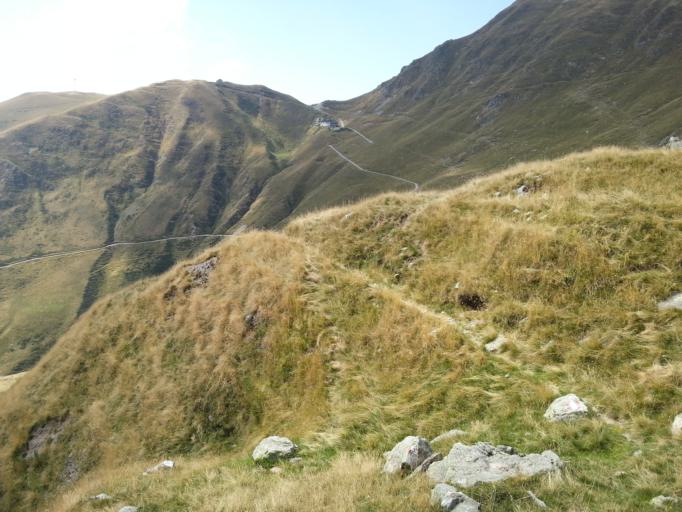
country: CH
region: Grisons
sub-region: Moesa District
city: Roveredo
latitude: 46.1662
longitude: 9.1697
